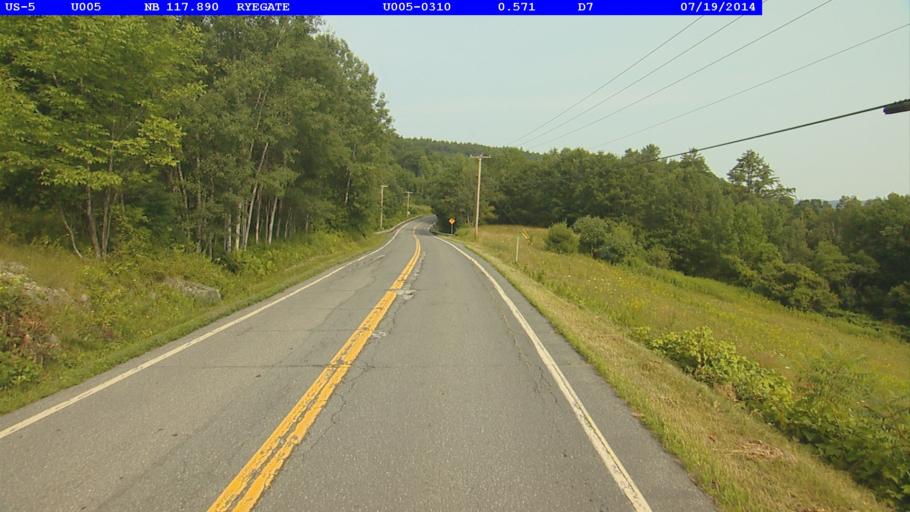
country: US
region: New Hampshire
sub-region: Grafton County
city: Woodsville
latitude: 44.1651
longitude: -72.0520
